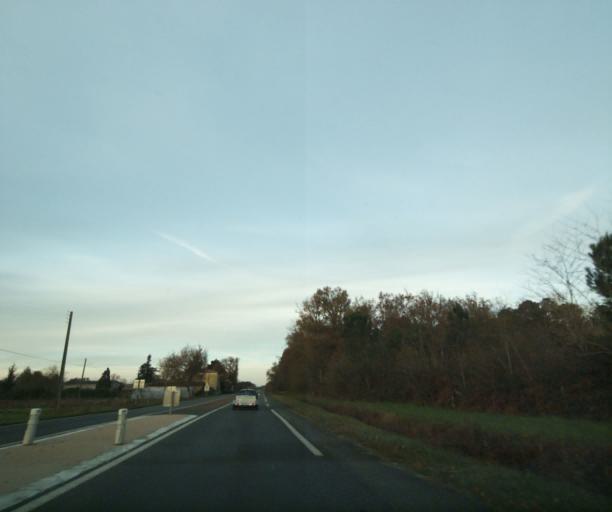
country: FR
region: Aquitaine
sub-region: Departement de la Gironde
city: Bazas
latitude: 44.4535
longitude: -0.2335
